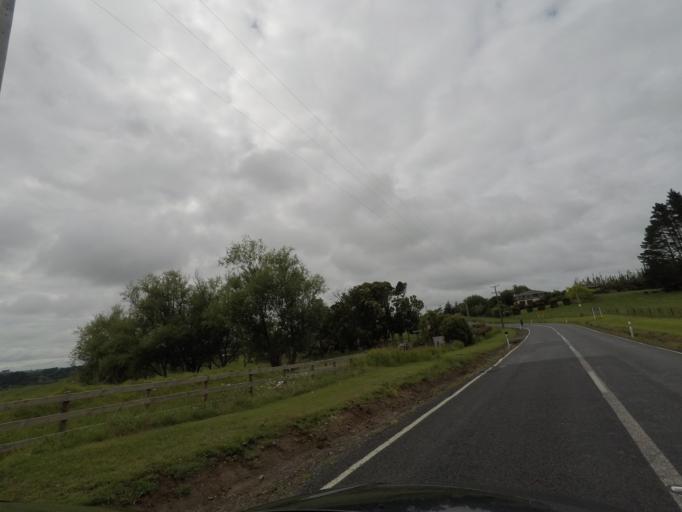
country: NZ
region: Auckland
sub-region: Auckland
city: Rosebank
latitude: -36.8014
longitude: 174.5737
